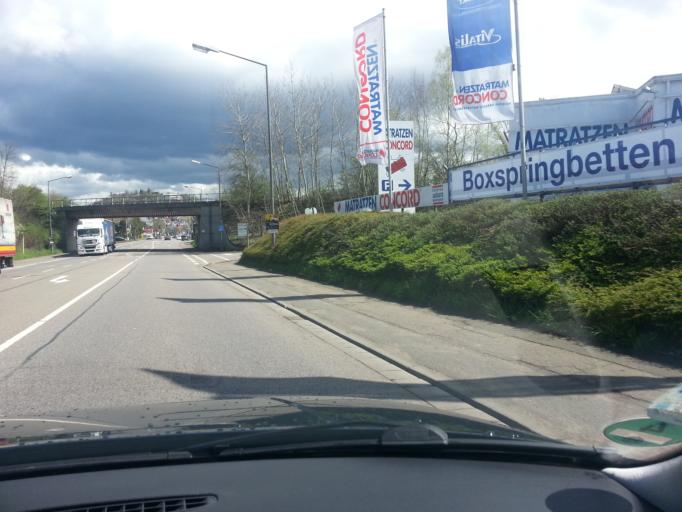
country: DE
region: Saarland
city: Homburg
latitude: 49.3185
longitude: 7.3241
